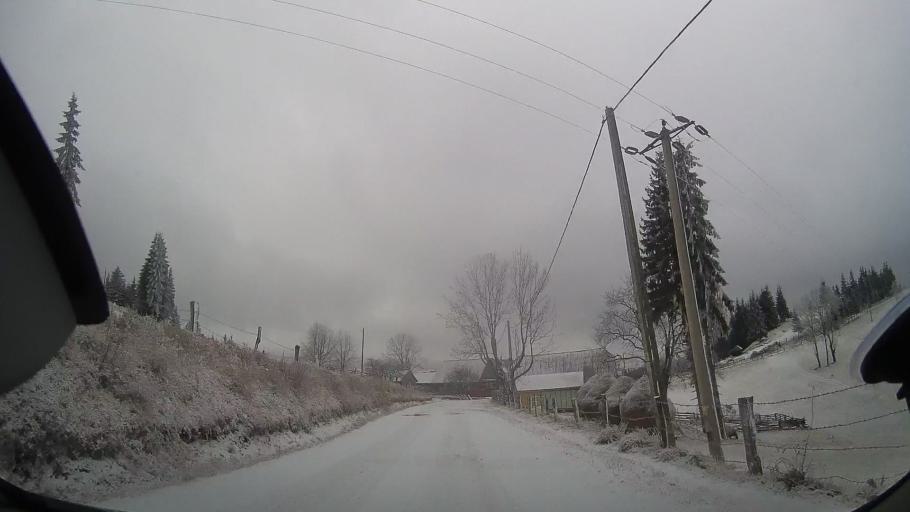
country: RO
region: Cluj
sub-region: Comuna Marisel
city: Marisel
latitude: 46.6578
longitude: 23.1395
